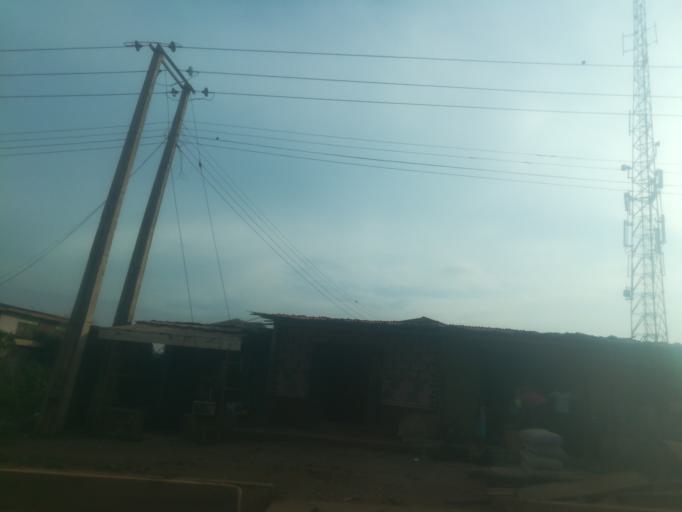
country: NG
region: Ogun
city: Abeokuta
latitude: 7.1666
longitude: 3.3036
